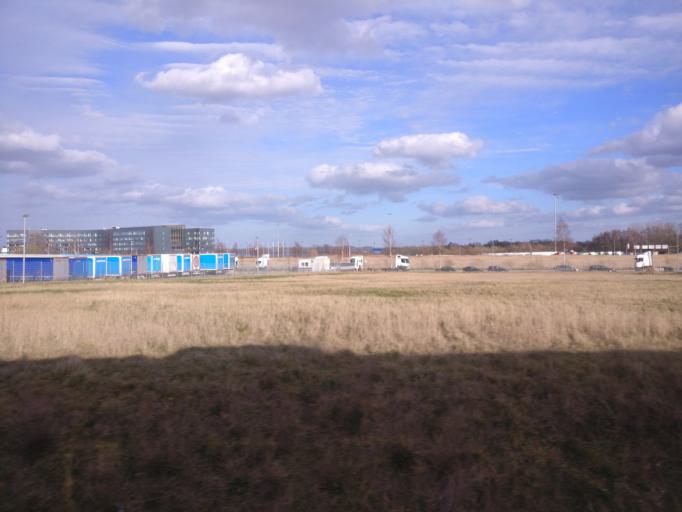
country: DE
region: Schleswig-Holstein
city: Travemuende
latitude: 53.9392
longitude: 10.8470
